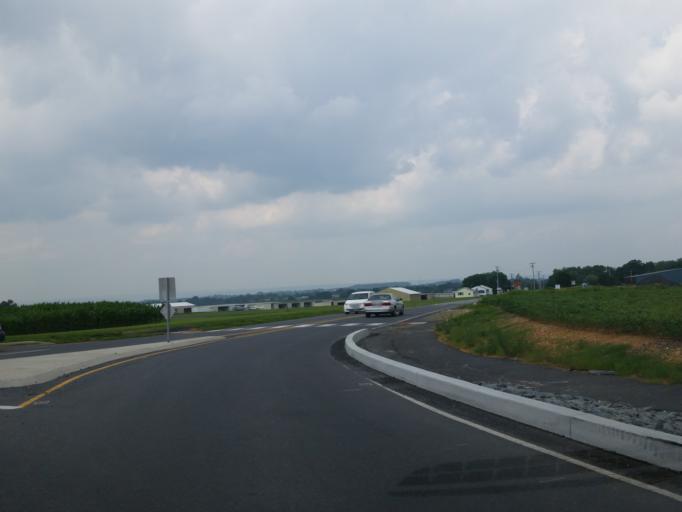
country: US
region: Pennsylvania
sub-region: Lebanon County
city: Campbelltown
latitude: 40.2850
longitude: -76.5734
